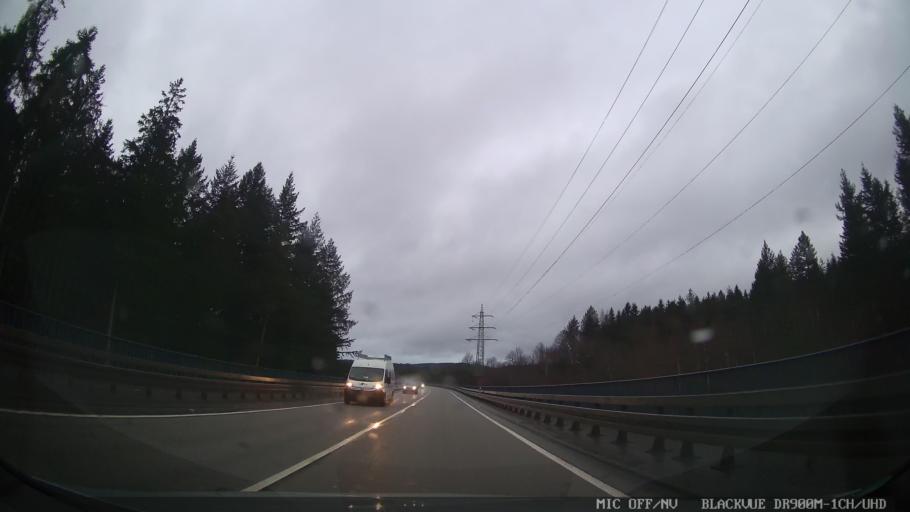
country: DE
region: Saarland
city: Mettlach
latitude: 49.4838
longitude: 6.6147
